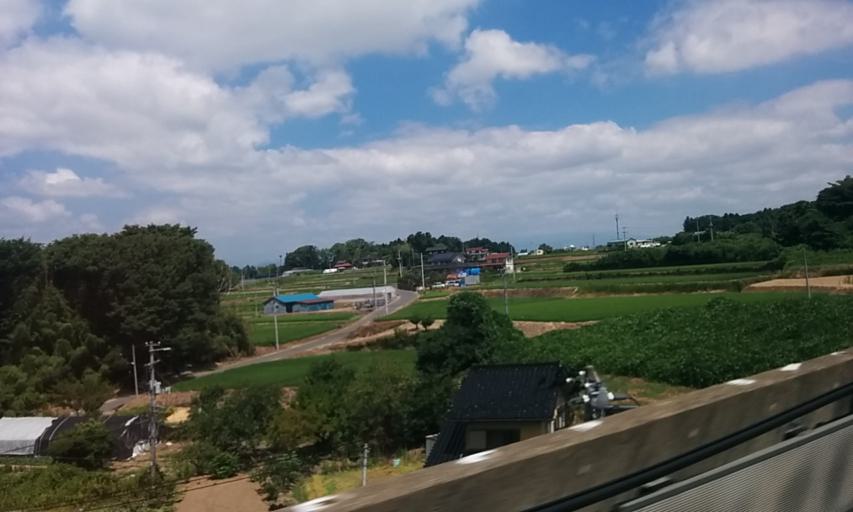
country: JP
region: Fukushima
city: Sukagawa
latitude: 37.3243
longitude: 140.3579
